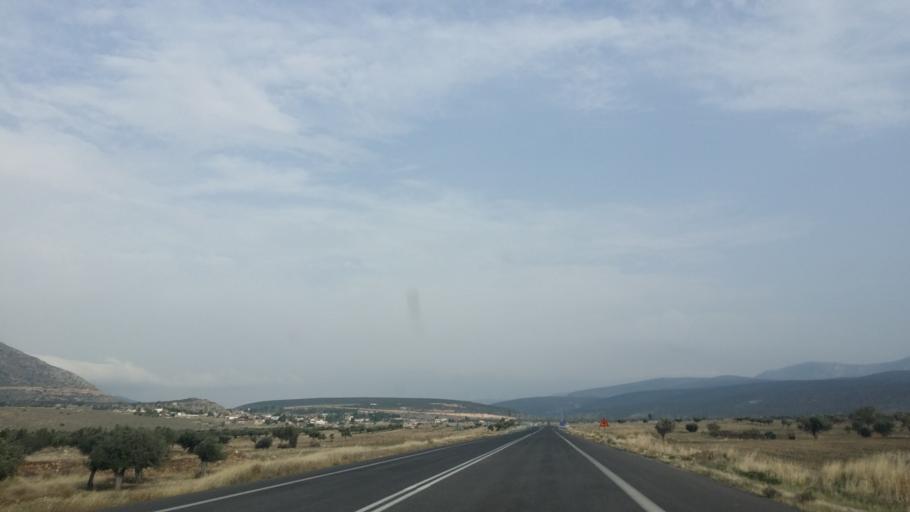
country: GR
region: Central Greece
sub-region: Nomos Voiotias
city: Korini
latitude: 38.2486
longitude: 22.9614
